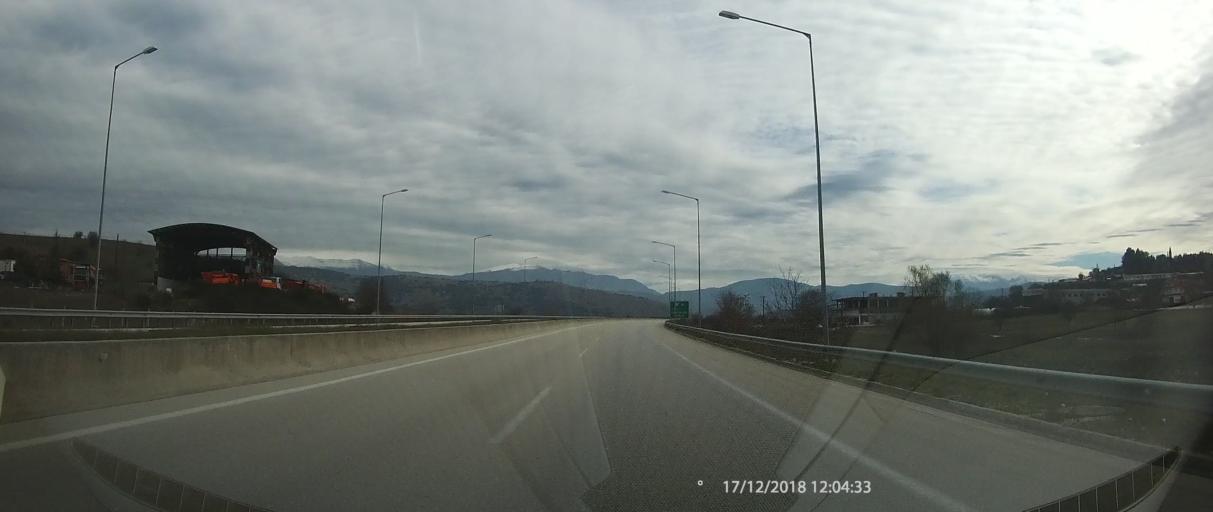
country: GR
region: Epirus
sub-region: Nomos Ioanninon
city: Katsikas
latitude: 39.6030
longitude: 20.8872
